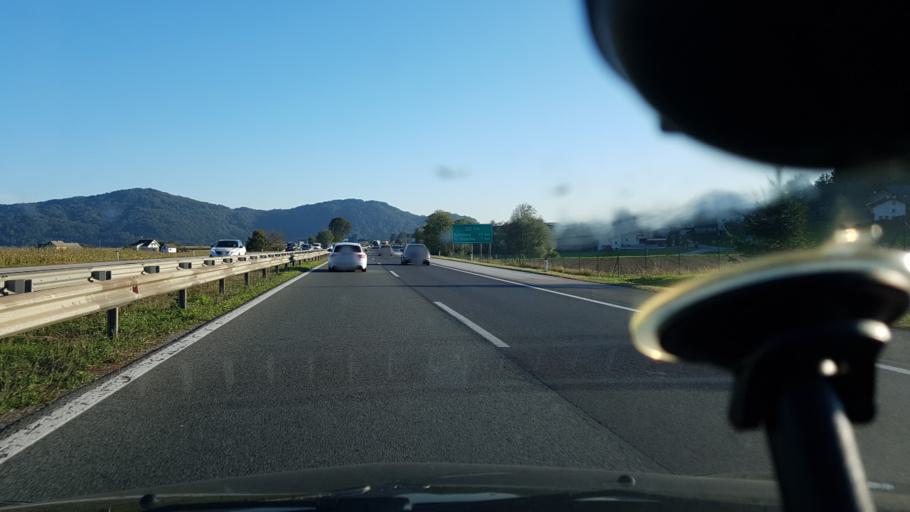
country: SI
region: Vodice
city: Vodice
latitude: 46.1790
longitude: 14.4854
